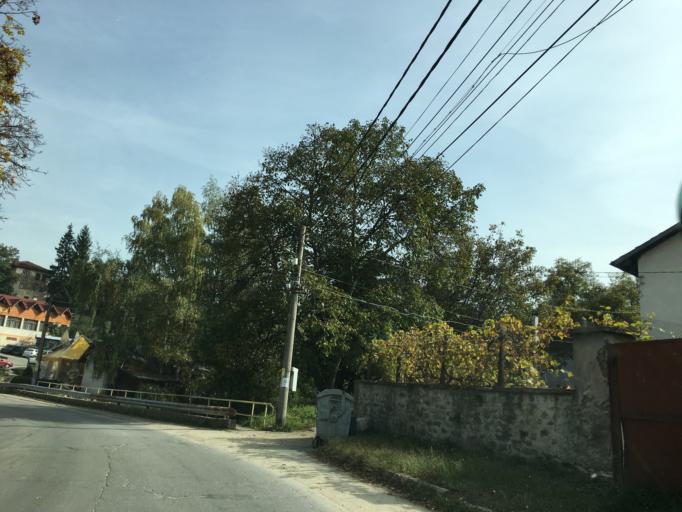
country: BG
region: Sofiya
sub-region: Obshtina Dolna Banya
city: Dolna Banya
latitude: 42.2864
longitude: 23.6877
